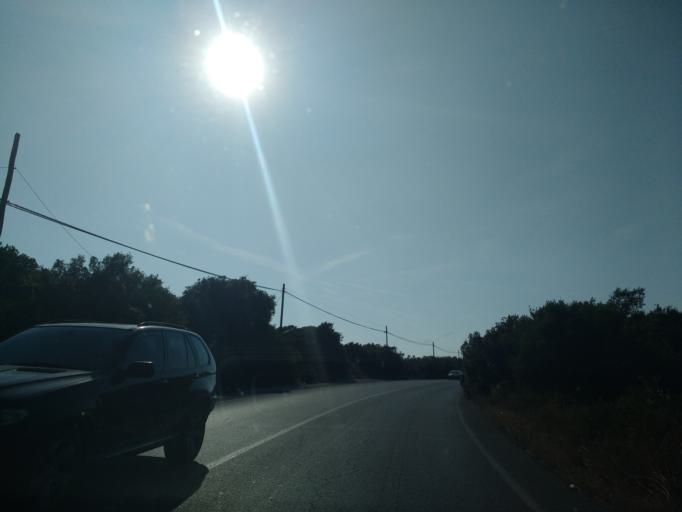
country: IT
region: Latium
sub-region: Citta metropolitana di Roma Capitale
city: Acilia-Castel Fusano-Ostia Antica
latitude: 41.6999
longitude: 12.3532
